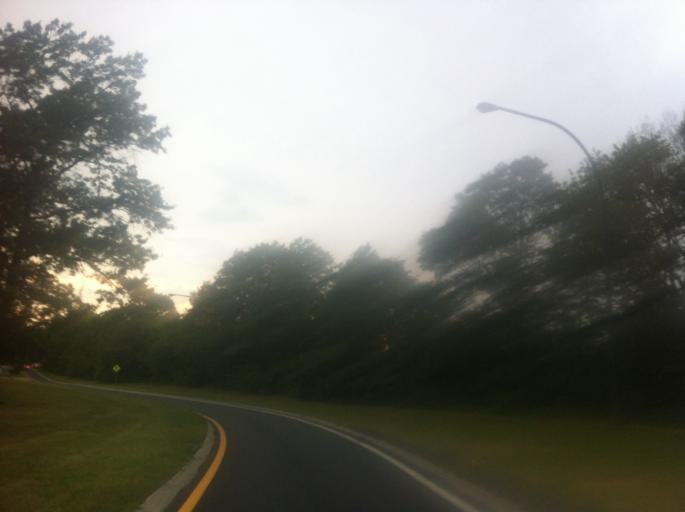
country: US
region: New York
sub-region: Nassau County
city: Jericho
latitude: 40.7911
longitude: -73.5172
